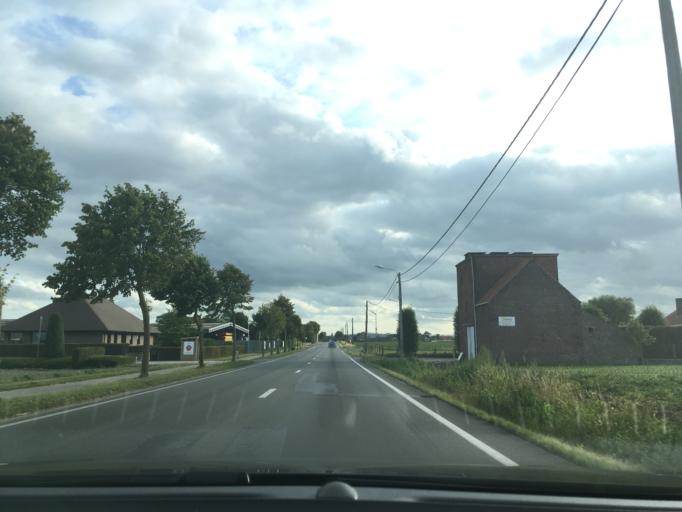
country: BE
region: Flanders
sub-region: Provincie West-Vlaanderen
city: Staden
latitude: 50.9530
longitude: 3.0443
